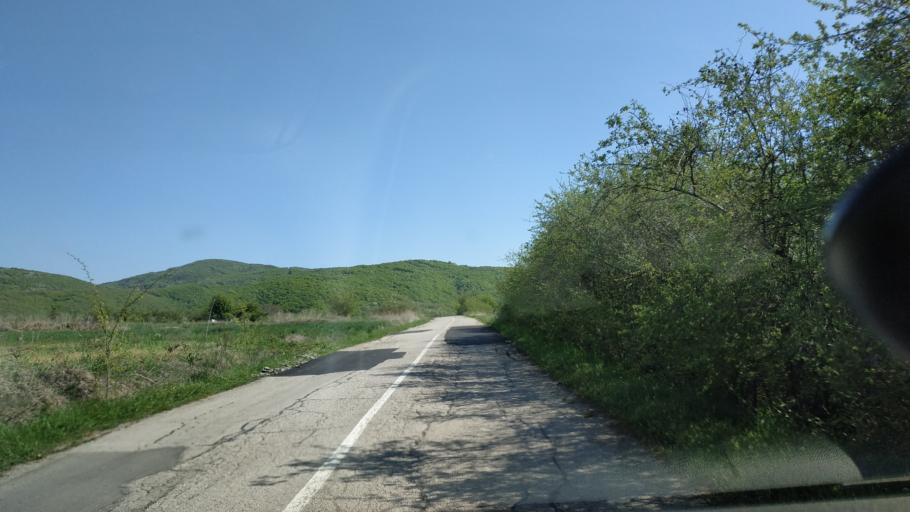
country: RS
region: Central Serbia
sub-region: Nisavski Okrug
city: Nis
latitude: 43.4326
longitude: 21.8477
